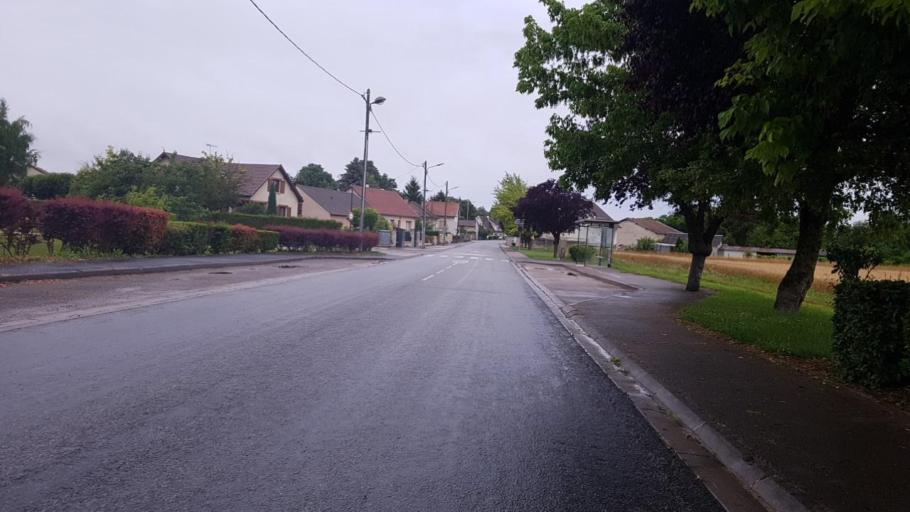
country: FR
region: Champagne-Ardenne
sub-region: Departement de la Marne
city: Sarry
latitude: 48.9046
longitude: 4.4320
